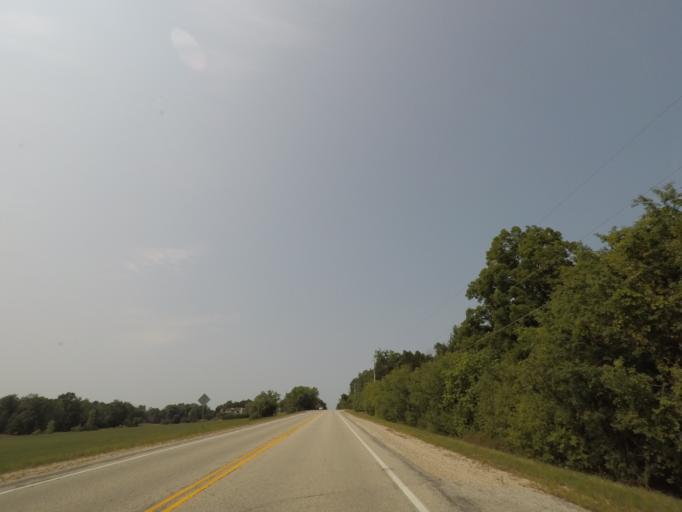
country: US
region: Wisconsin
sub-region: Waukesha County
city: Oconomowoc
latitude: 43.0619
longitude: -88.4947
